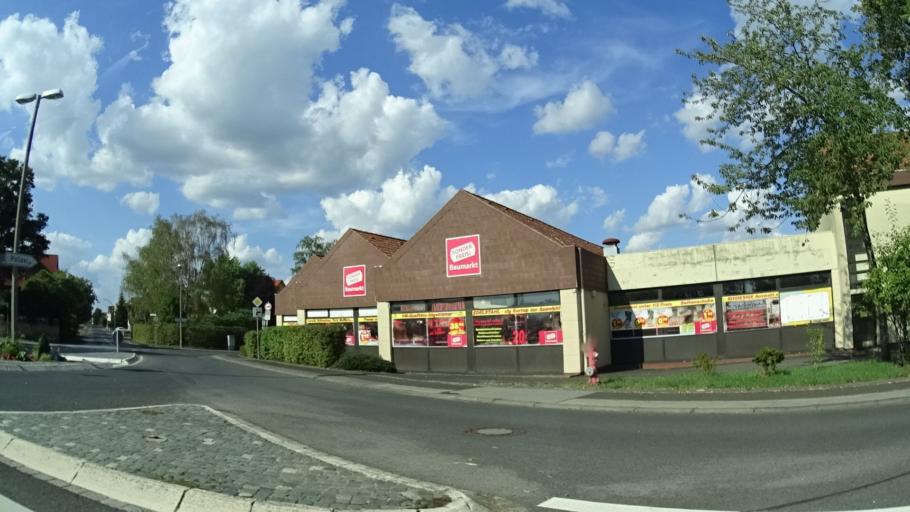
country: DE
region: Bavaria
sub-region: Regierungsbezirk Unterfranken
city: Bad Konigshofen im Grabfeld
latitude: 50.2991
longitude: 10.4611
